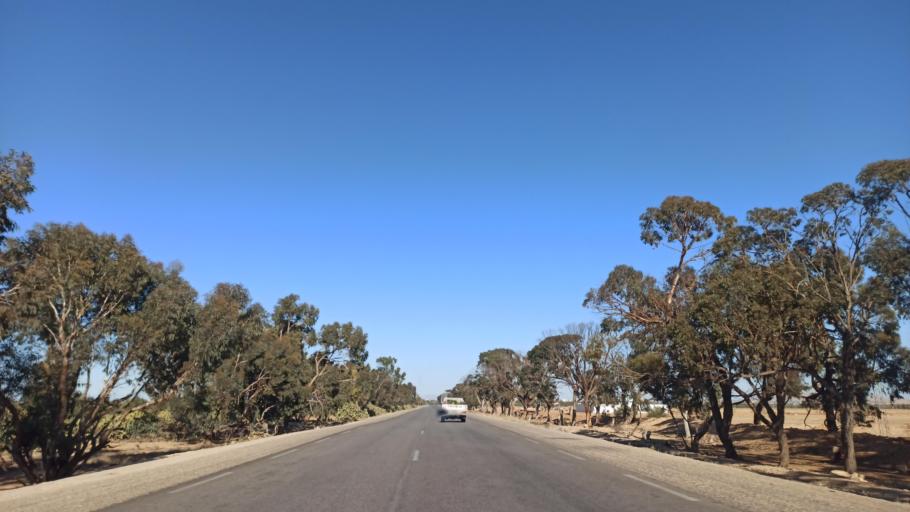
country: TN
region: Sidi Bu Zayd
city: Jilma
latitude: 35.2336
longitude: 9.3861
